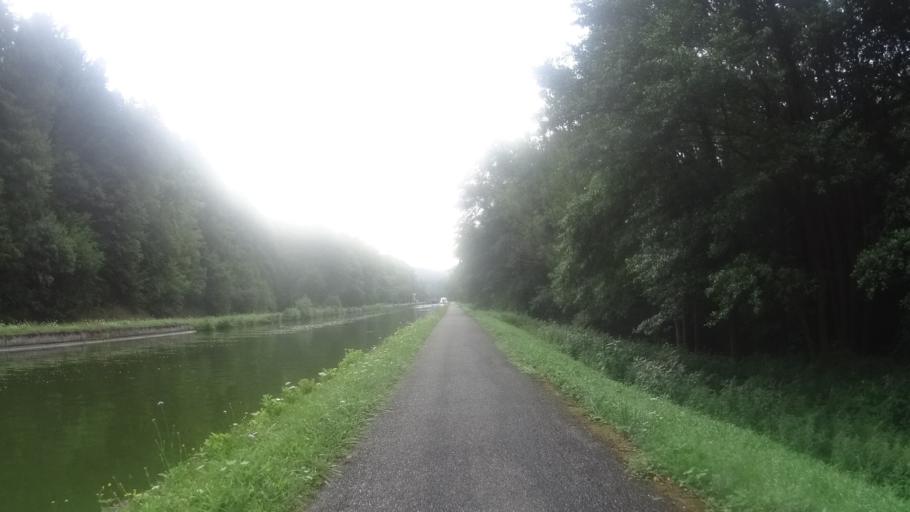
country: FR
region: Lorraine
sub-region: Departement de la Moselle
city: Phalsbourg
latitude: 48.7347
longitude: 7.2778
